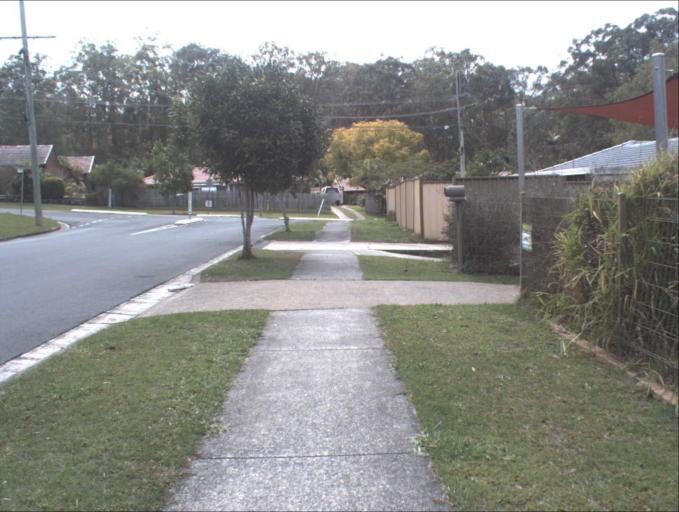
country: AU
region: Queensland
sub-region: Brisbane
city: Sunnybank Hills
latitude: -27.6557
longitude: 153.0439
